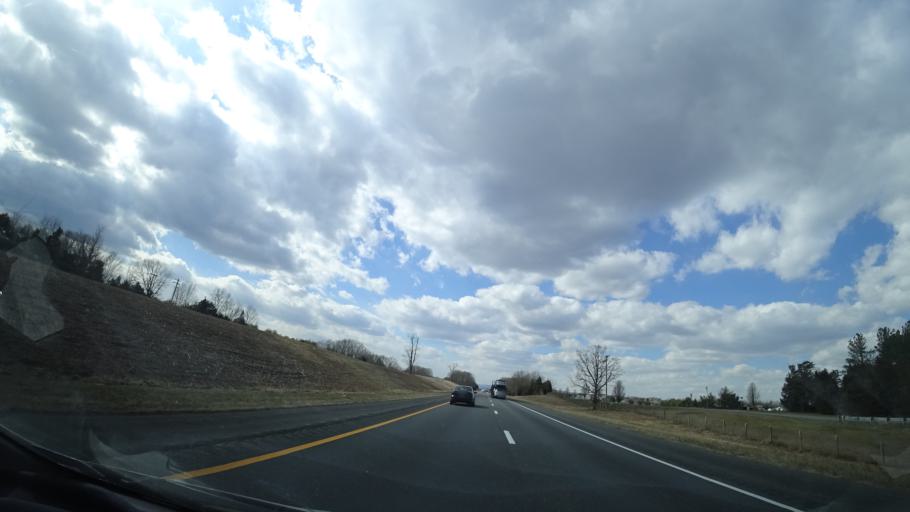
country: US
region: Virginia
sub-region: Warren County
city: Front Royal
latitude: 38.9781
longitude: -78.2216
